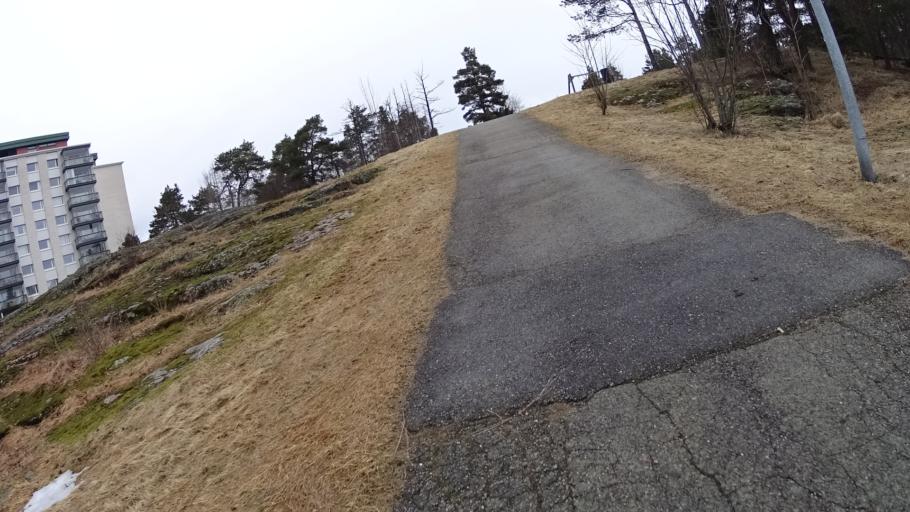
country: FI
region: Uusimaa
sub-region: Helsinki
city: Teekkarikylae
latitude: 60.2282
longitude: 24.8527
